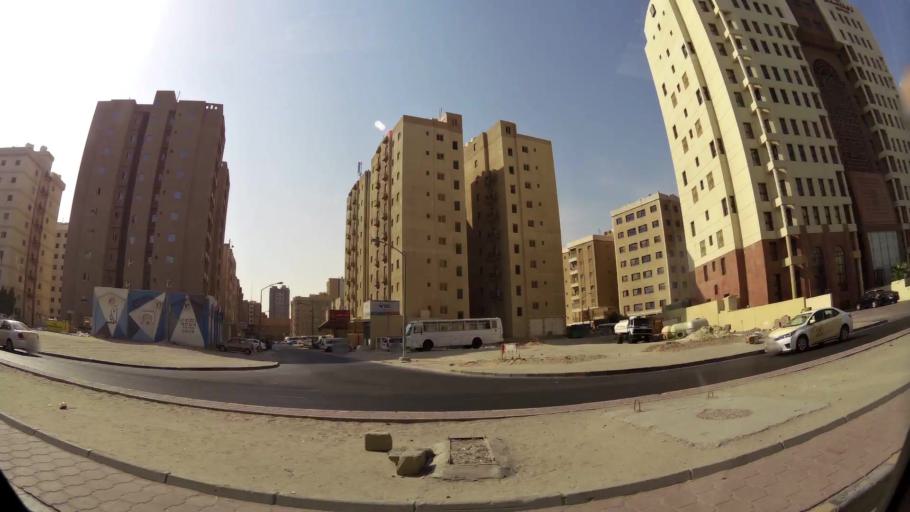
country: KW
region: Al Ahmadi
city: Al Fintas
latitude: 29.1582
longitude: 48.1163
